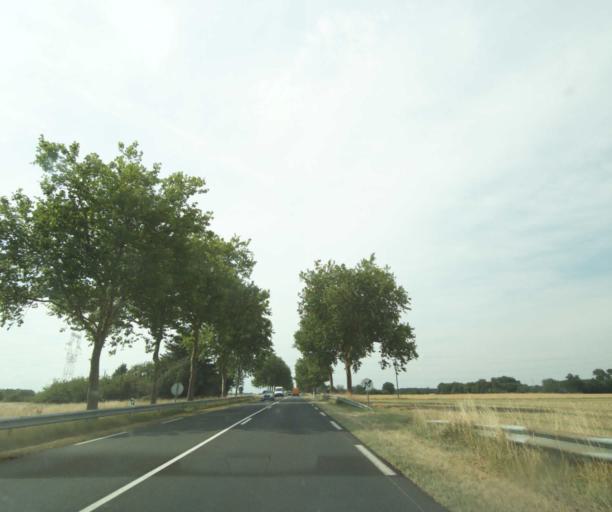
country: FR
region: Centre
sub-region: Departement d'Indre-et-Loire
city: Saint-Antoine-du-Rocher
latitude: 47.5100
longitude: 0.5930
